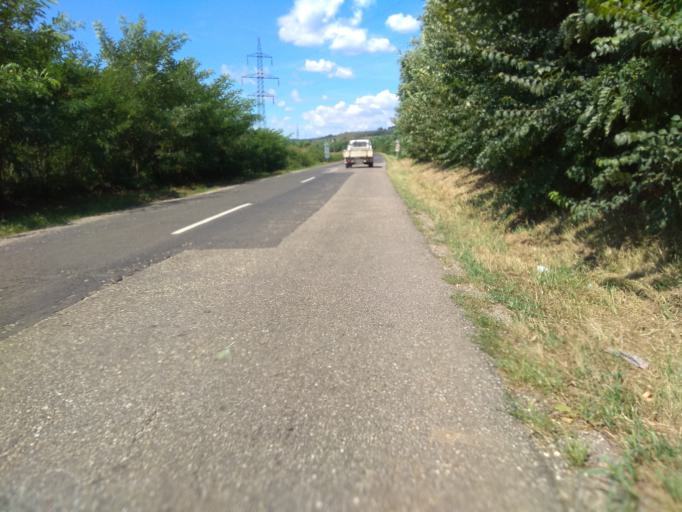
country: HU
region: Borsod-Abauj-Zemplen
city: Sajokaza
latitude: 48.2867
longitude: 20.6172
